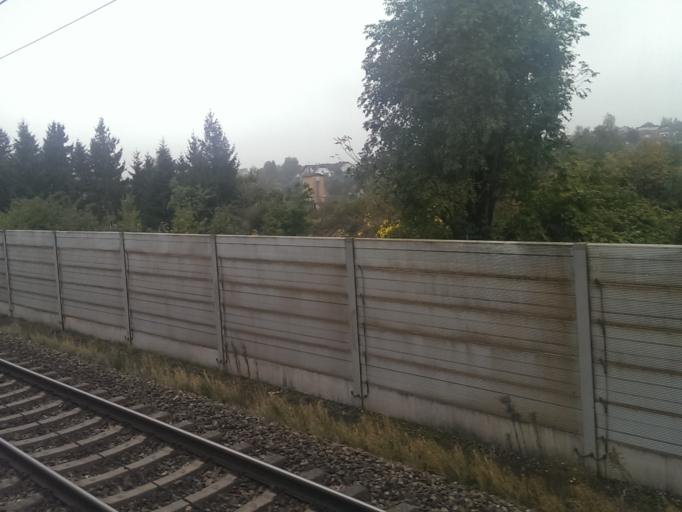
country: AT
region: Upper Austria
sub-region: Wels-Land
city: Lambach
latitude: 48.0945
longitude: 13.8687
